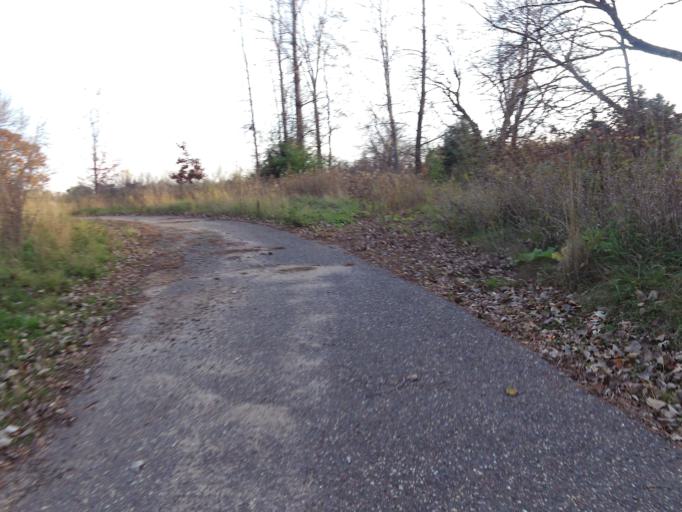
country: US
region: Minnesota
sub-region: Washington County
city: Lake Elmo
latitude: 44.9703
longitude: -92.8779
